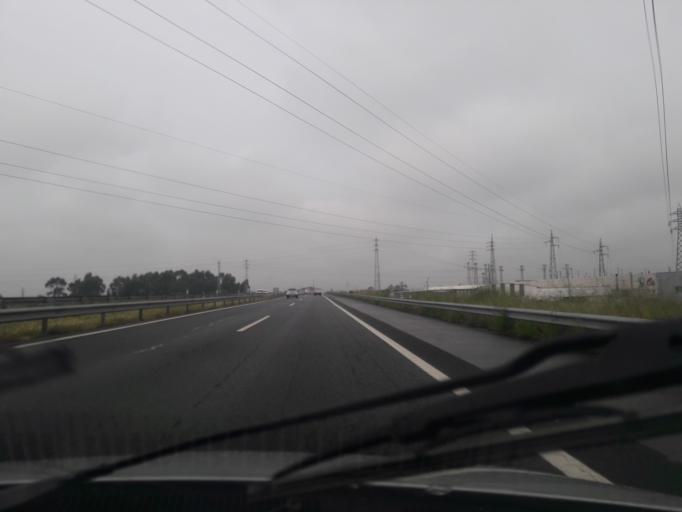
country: PT
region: Porto
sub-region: Povoa de Varzim
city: Pedroso
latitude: 41.3927
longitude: -8.7435
